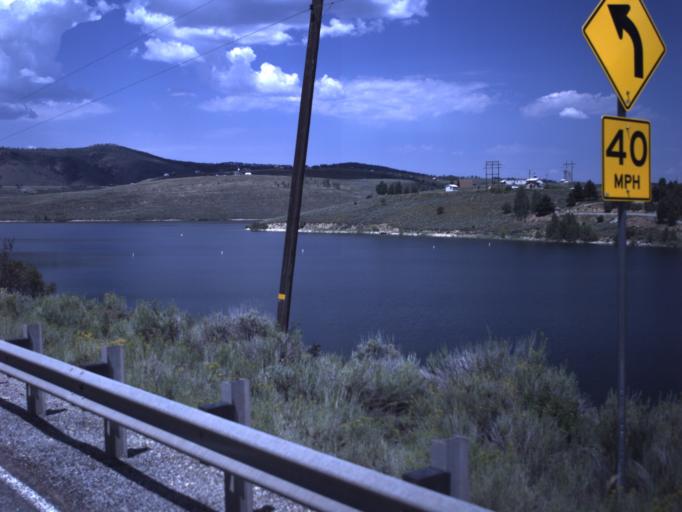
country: US
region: Utah
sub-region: Carbon County
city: Helper
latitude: 39.7871
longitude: -111.1292
